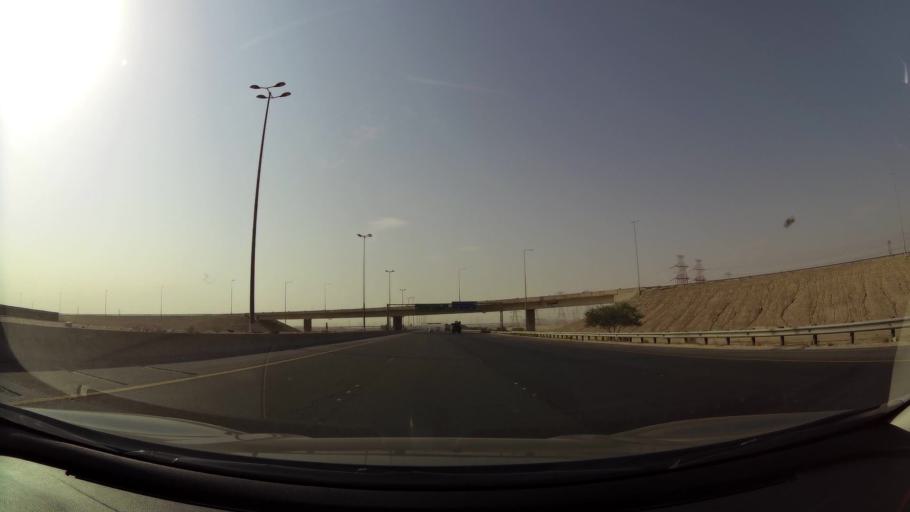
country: KW
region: Al Ahmadi
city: Al Ahmadi
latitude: 29.0488
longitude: 48.0951
